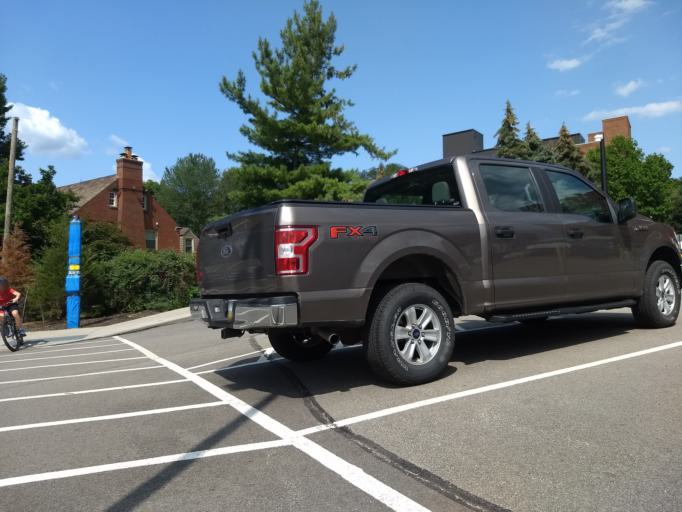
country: US
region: Pennsylvania
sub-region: Allegheny County
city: Bloomfield
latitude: 40.4460
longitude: -79.9438
